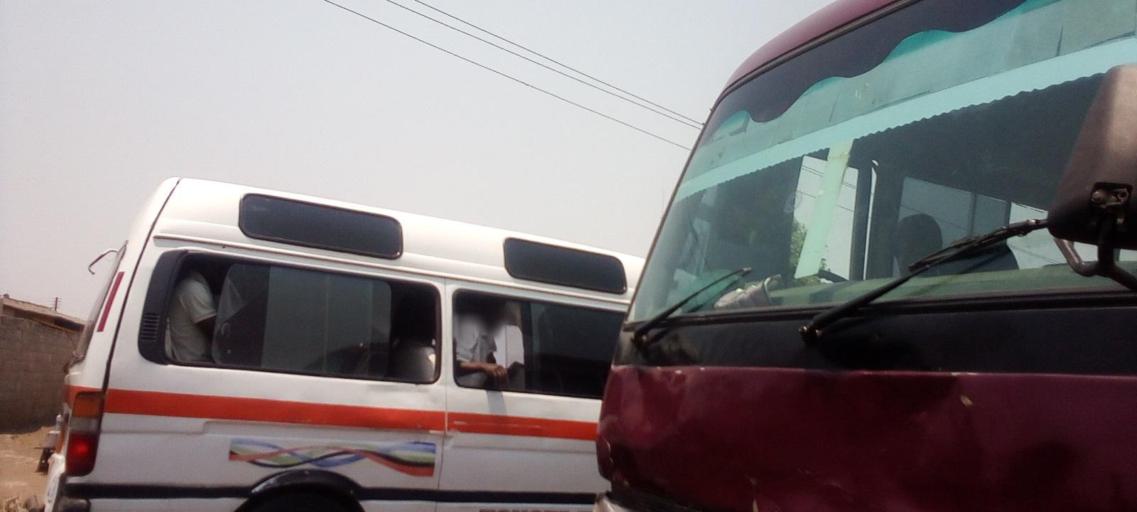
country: ZM
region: Lusaka
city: Lusaka
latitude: -15.4411
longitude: 28.2523
